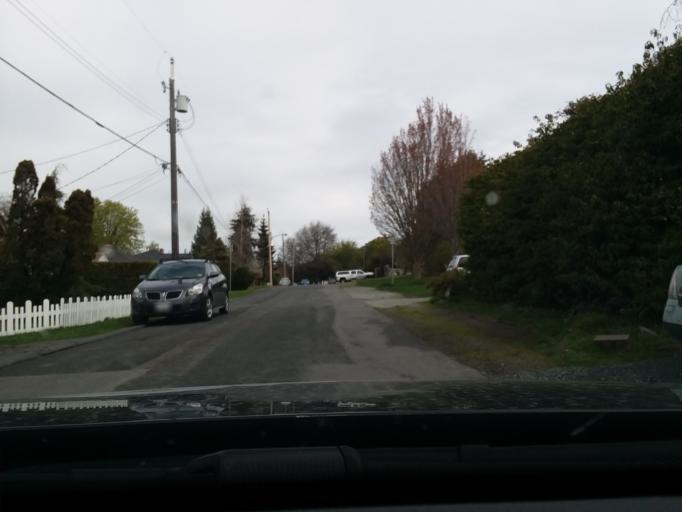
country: CA
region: British Columbia
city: Oak Bay
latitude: 48.4466
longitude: -123.3272
